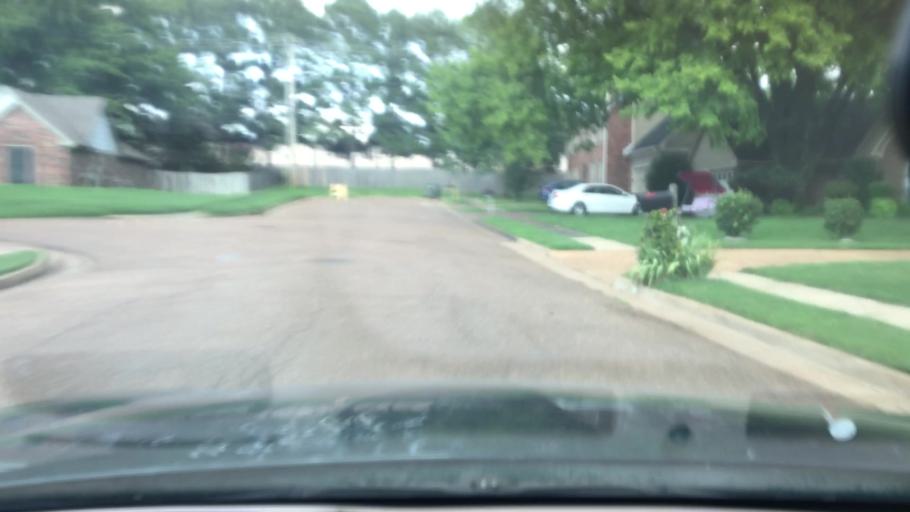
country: US
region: Tennessee
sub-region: Shelby County
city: Lakeland
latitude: 35.1942
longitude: -89.7996
